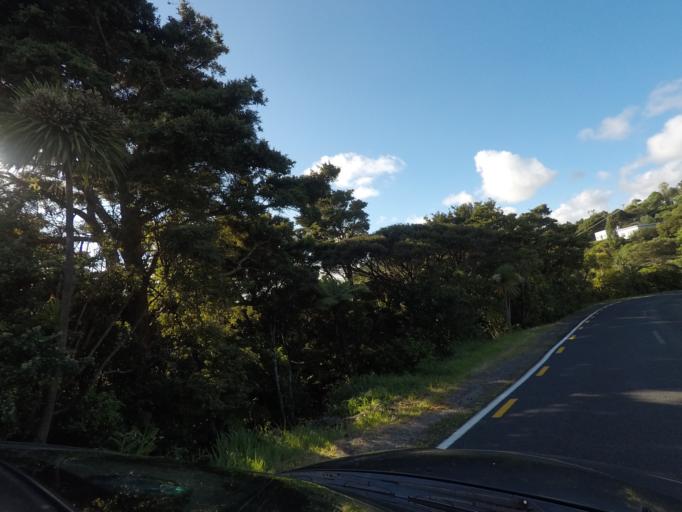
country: NZ
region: Auckland
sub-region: Auckland
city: Titirangi
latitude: -37.0099
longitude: 174.6034
